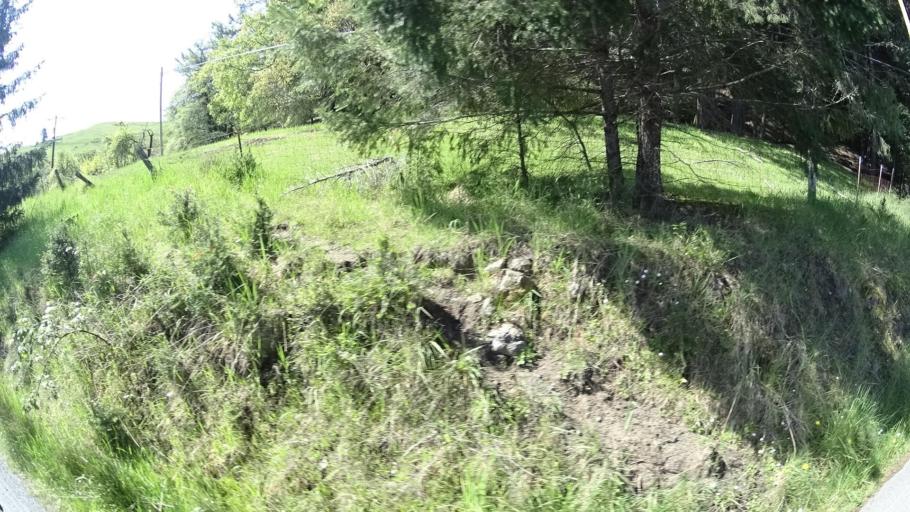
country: US
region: California
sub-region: Humboldt County
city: Redway
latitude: 40.0847
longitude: -123.6601
